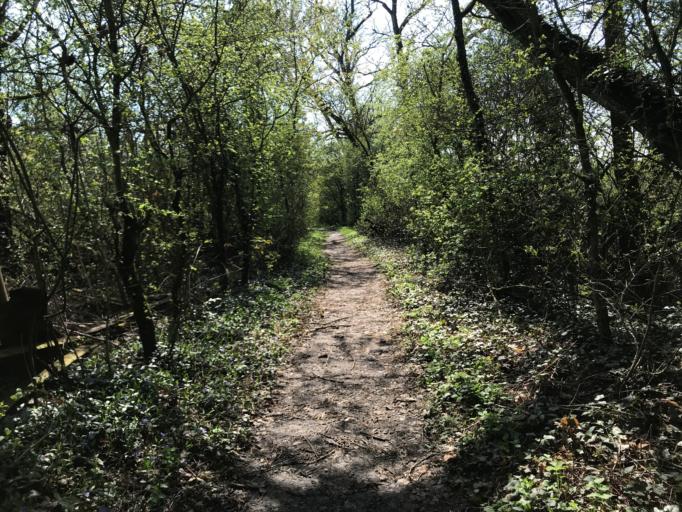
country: DE
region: Rheinland-Pfalz
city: Bodenheim
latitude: 49.9547
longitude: 8.3209
